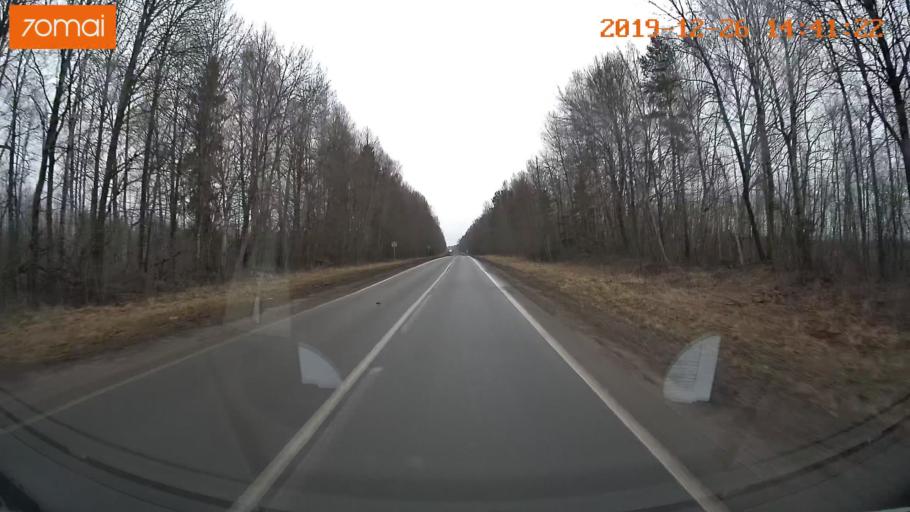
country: RU
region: Jaroslavl
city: Poshekhon'ye
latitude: 58.3720
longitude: 39.0182
